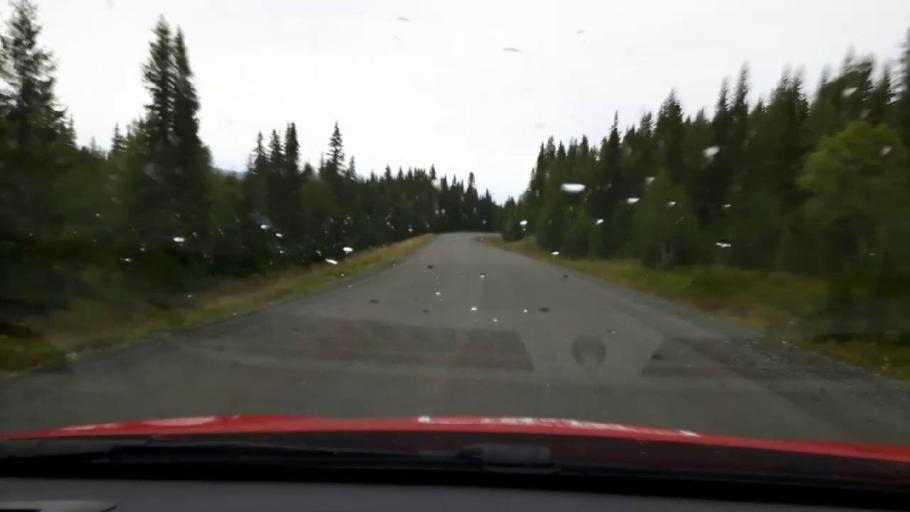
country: SE
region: Jaemtland
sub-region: Are Kommun
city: Are
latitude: 63.4214
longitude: 12.7490
